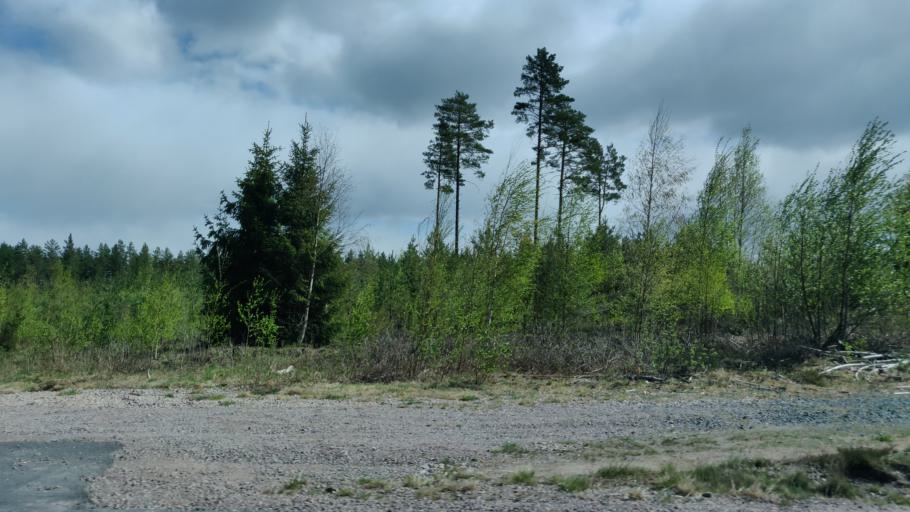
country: SE
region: Vaermland
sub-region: Hagfors Kommun
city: Hagfors
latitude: 59.8703
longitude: 13.7078
